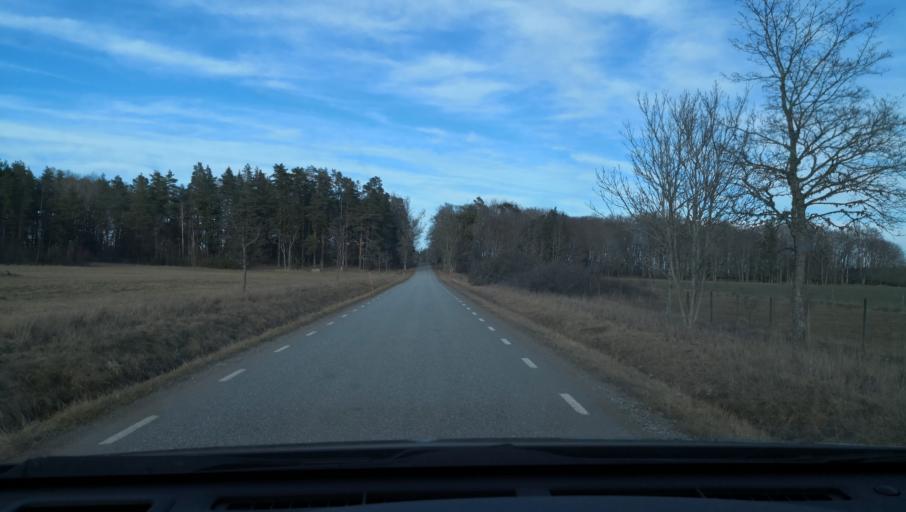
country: SE
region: Uppsala
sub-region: Enkopings Kommun
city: Grillby
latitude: 59.5460
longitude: 17.2095
